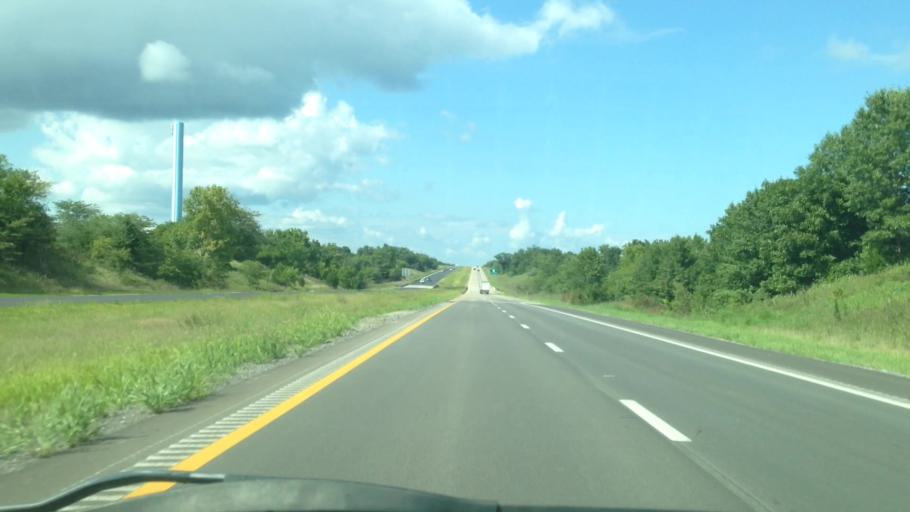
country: US
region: Missouri
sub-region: Lewis County
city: Canton
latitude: 40.0241
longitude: -91.5259
